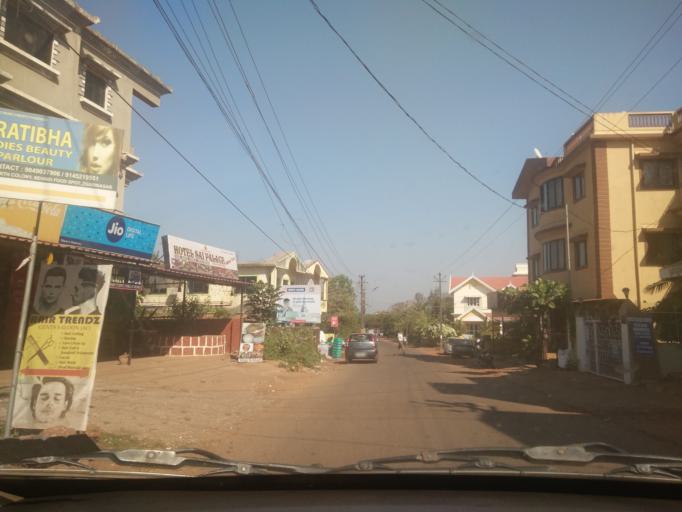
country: IN
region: Goa
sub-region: South Goa
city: Chicalim
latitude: 15.3901
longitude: 73.8640
